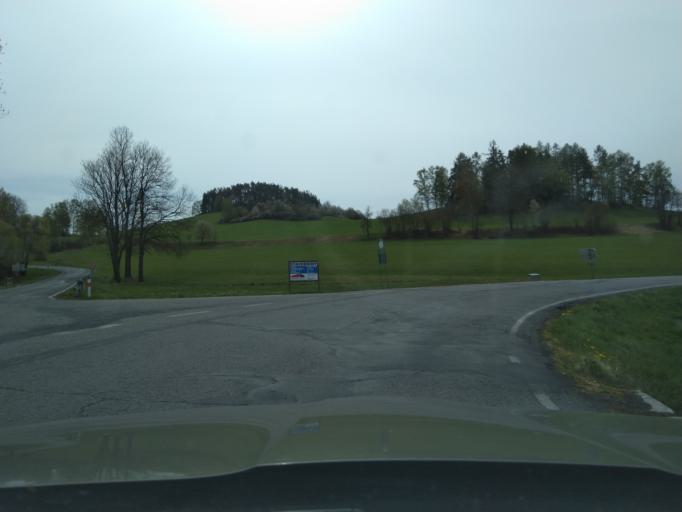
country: CZ
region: Plzensky
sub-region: Okres Klatovy
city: Susice
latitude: 49.2200
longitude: 13.6142
